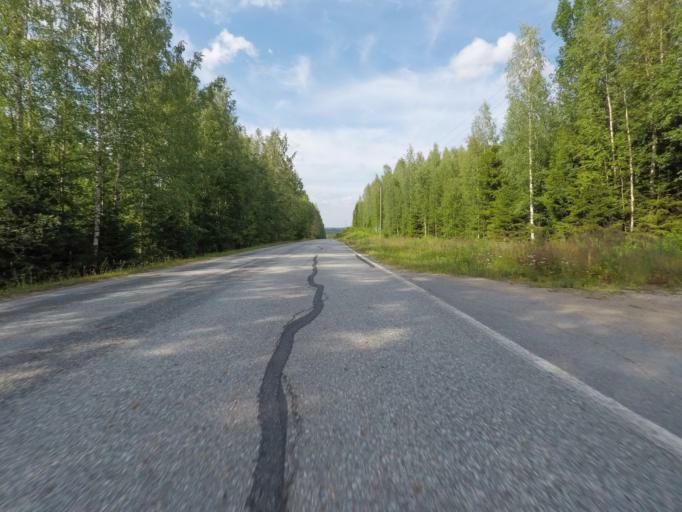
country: FI
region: Southern Savonia
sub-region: Savonlinna
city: Sulkava
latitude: 61.7107
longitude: 28.2103
